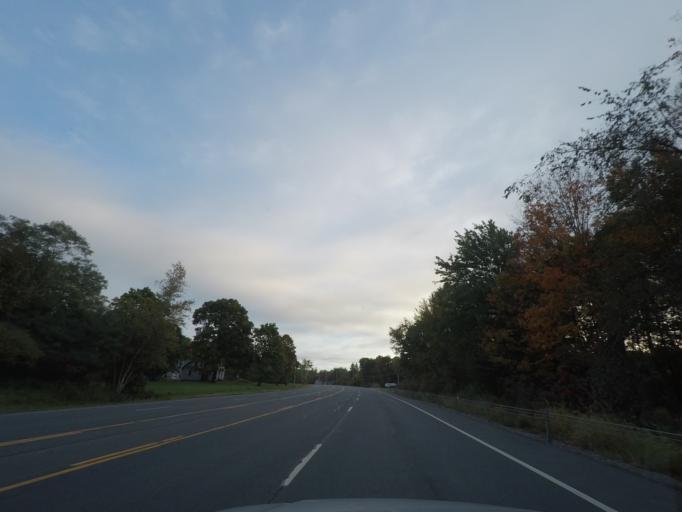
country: US
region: New York
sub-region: Rensselaer County
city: East Greenbush
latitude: 42.5375
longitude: -73.6786
